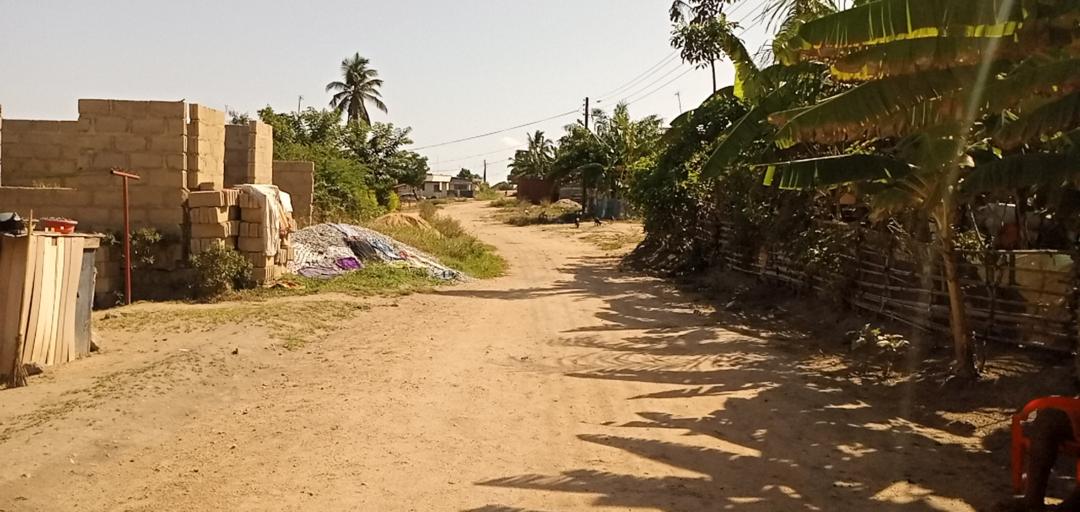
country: GH
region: Central
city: Winneba
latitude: 5.3543
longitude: -0.6222
